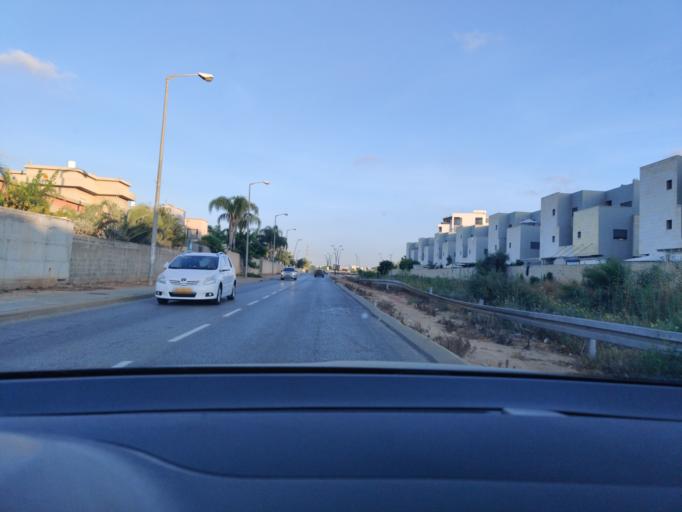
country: IL
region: Central District
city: Elyakhin
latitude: 32.4289
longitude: 34.9402
